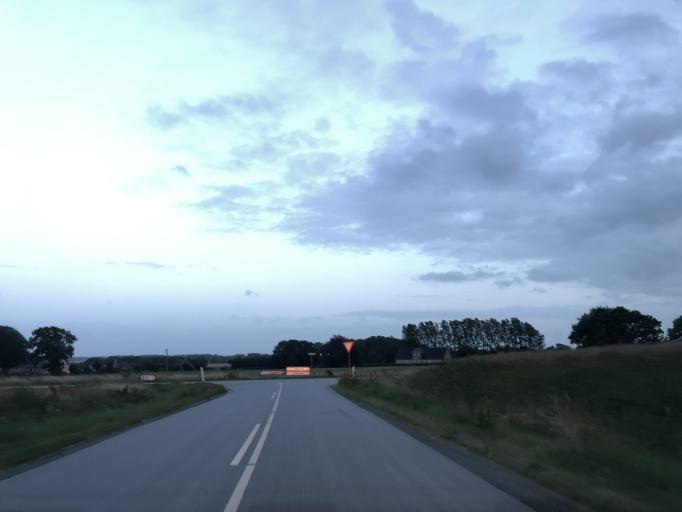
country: DK
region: South Denmark
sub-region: Haderslev Kommune
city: Starup
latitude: 55.2309
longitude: 9.6378
